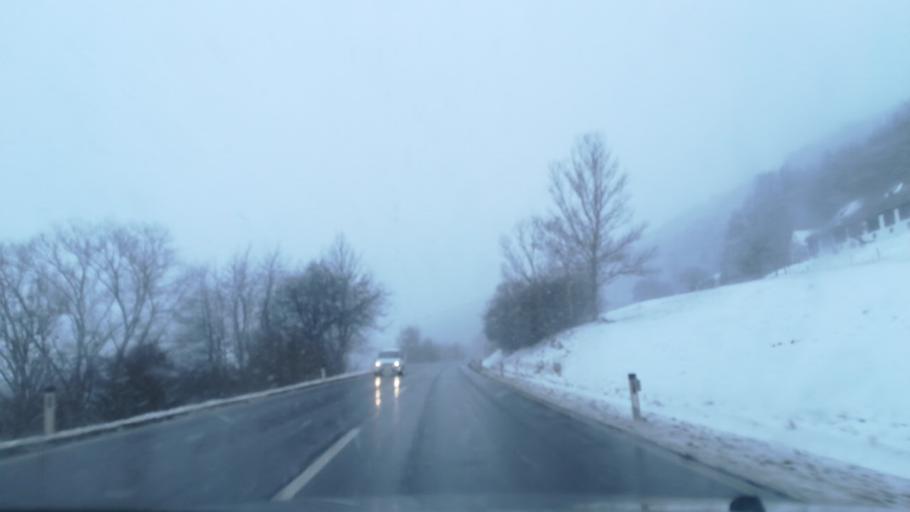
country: AT
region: Styria
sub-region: Politischer Bezirk Murtal
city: Sankt Peter ob Judenburg
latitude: 47.2004
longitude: 14.5894
